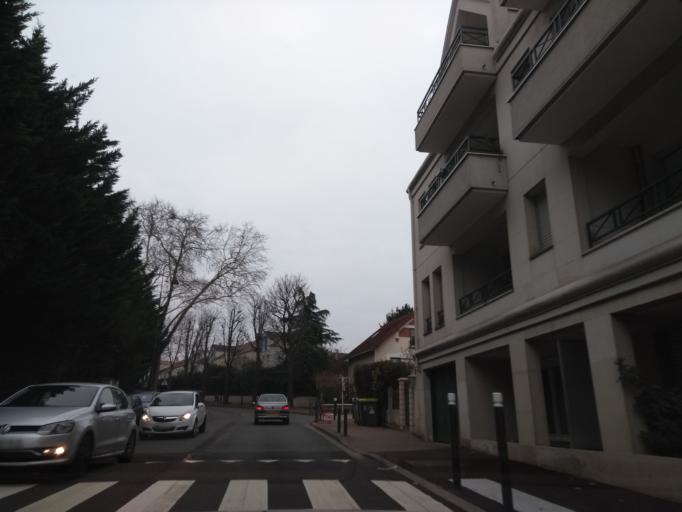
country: FR
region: Ile-de-France
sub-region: Departement des Hauts-de-Seine
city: Antony
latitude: 48.7565
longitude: 2.2951
